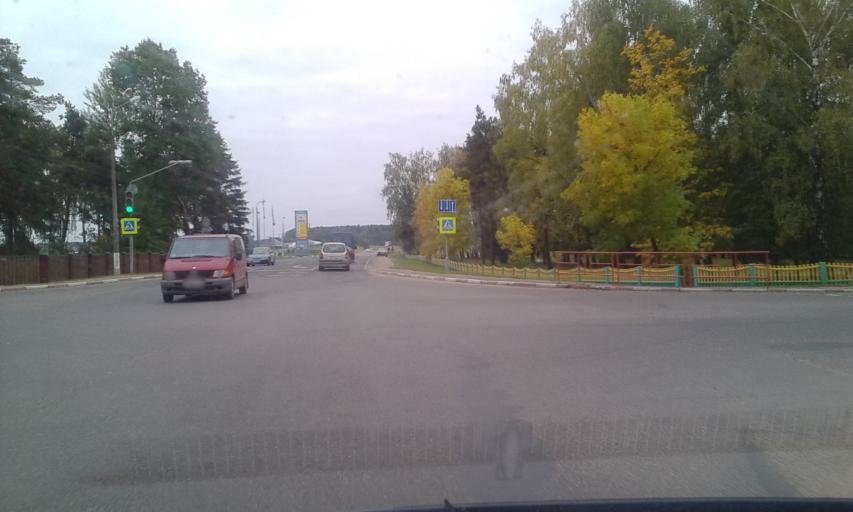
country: BY
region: Vitebsk
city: Pastavy
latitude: 55.1126
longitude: 26.8727
